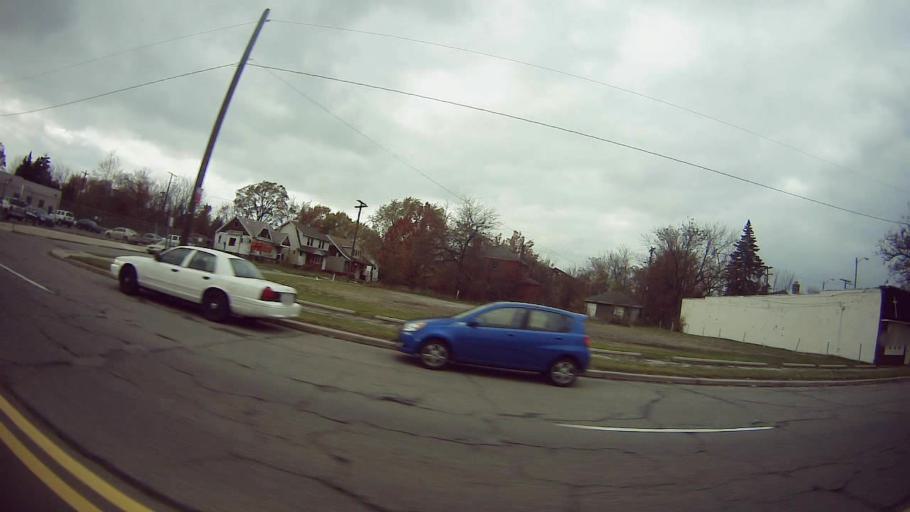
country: US
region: Michigan
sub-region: Macomb County
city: Eastpointe
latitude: 42.4262
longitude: -82.9865
